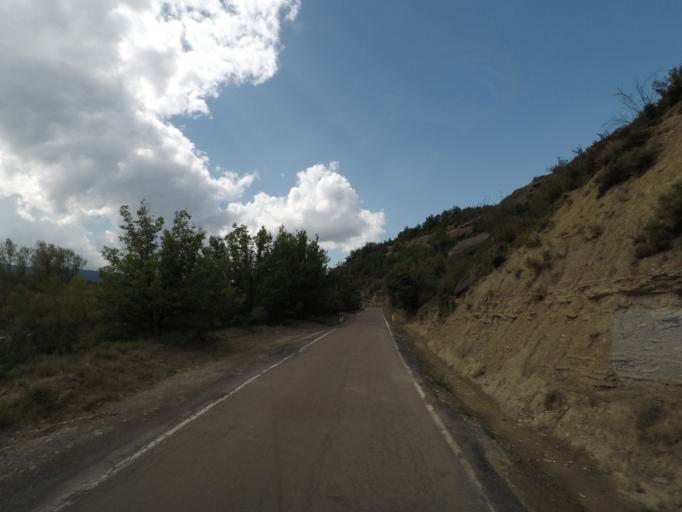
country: ES
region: Aragon
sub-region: Provincia de Huesca
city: Yebra de Basa
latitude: 42.3907
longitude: -0.2779
